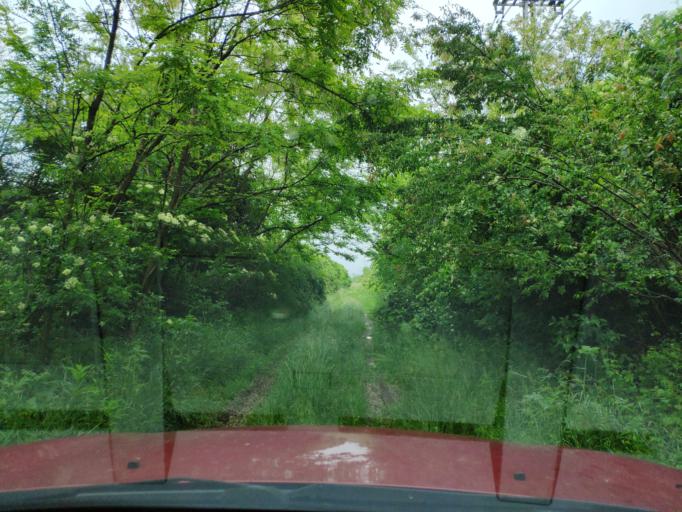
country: SK
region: Kosicky
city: Cierna nad Tisou
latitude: 48.4261
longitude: 22.0759
